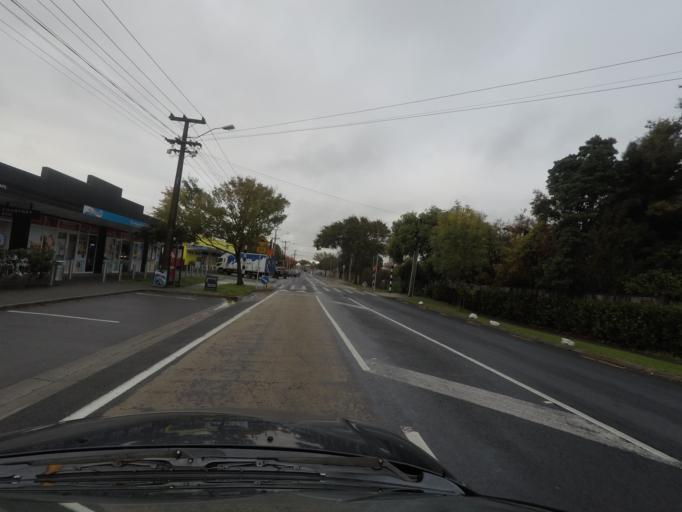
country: NZ
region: Auckland
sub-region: Auckland
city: Rosebank
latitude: -36.7564
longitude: 174.5917
